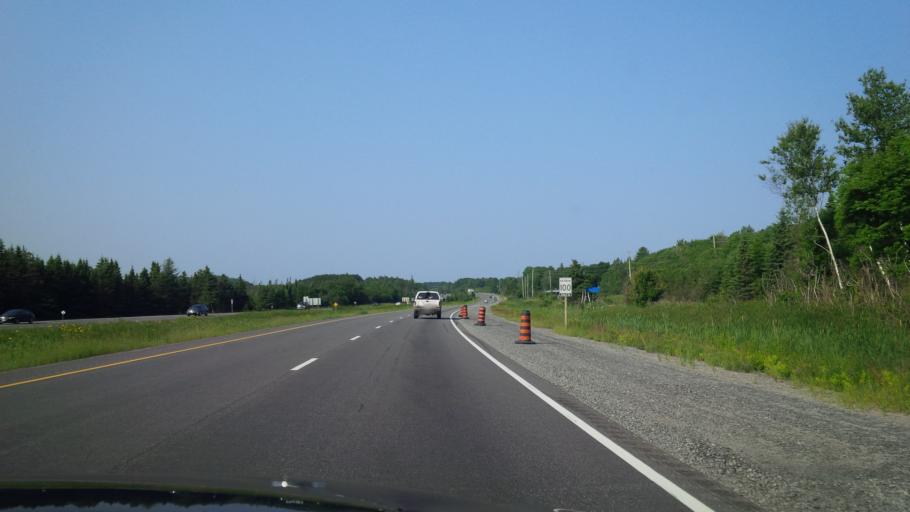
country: CA
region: Ontario
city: Huntsville
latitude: 45.3025
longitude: -79.2513
